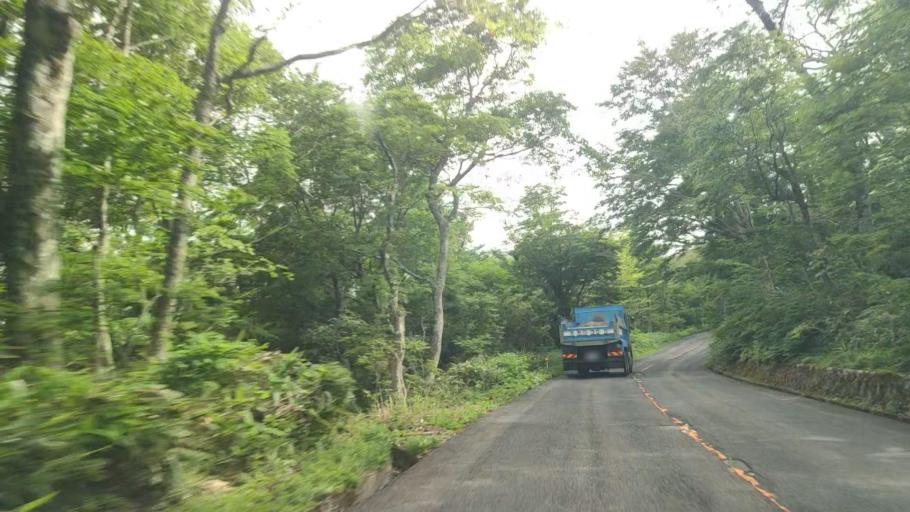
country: JP
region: Tottori
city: Yonago
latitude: 35.3853
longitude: 133.5260
